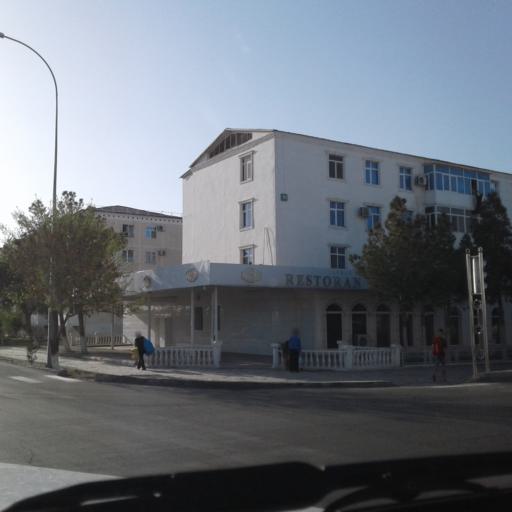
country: TM
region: Lebap
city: Turkmenabat
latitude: 39.0943
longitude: 63.5744
